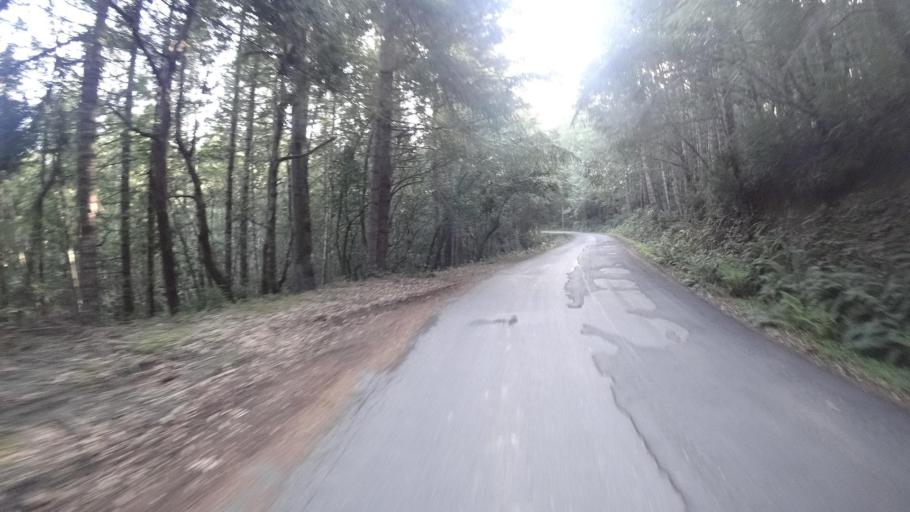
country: US
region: California
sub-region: Humboldt County
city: Blue Lake
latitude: 40.7019
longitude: -123.9404
